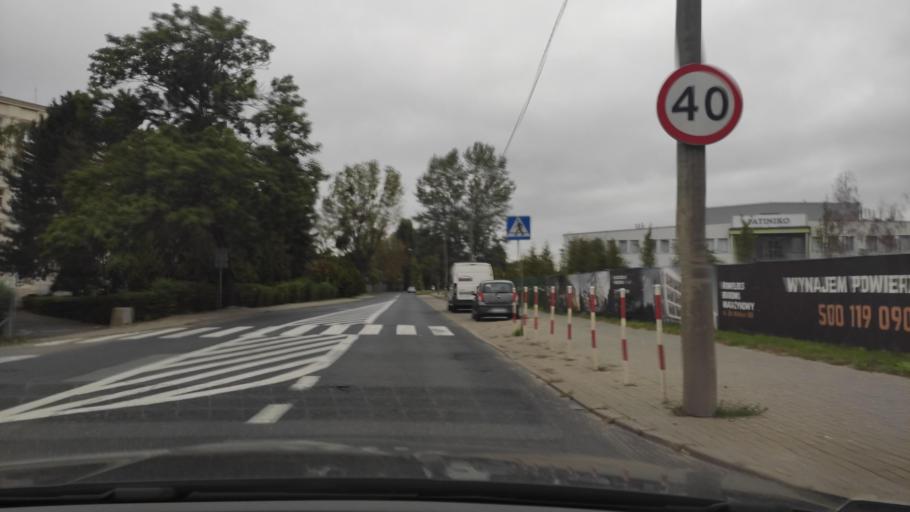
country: PL
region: Greater Poland Voivodeship
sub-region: Poznan
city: Poznan
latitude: 52.4137
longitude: 16.9774
